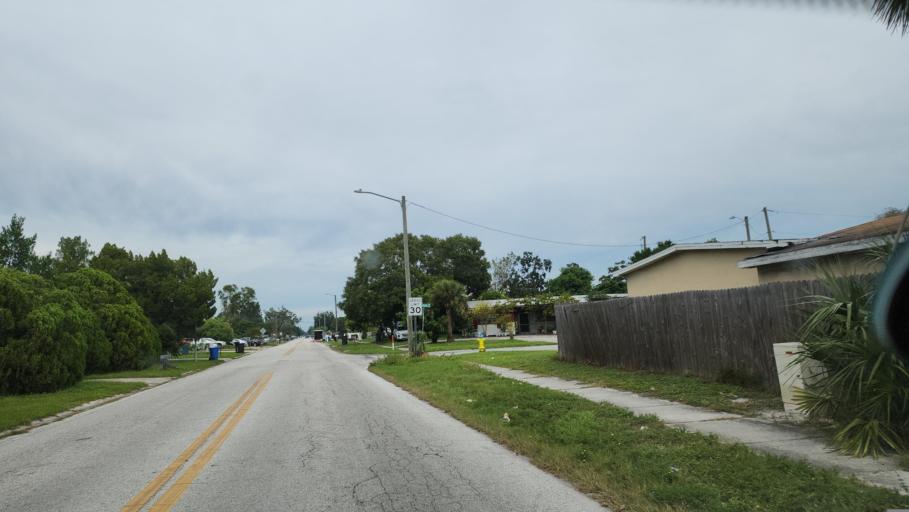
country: US
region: Florida
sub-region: Hillsborough County
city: Town 'n' Country
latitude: 27.9858
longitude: -82.5690
